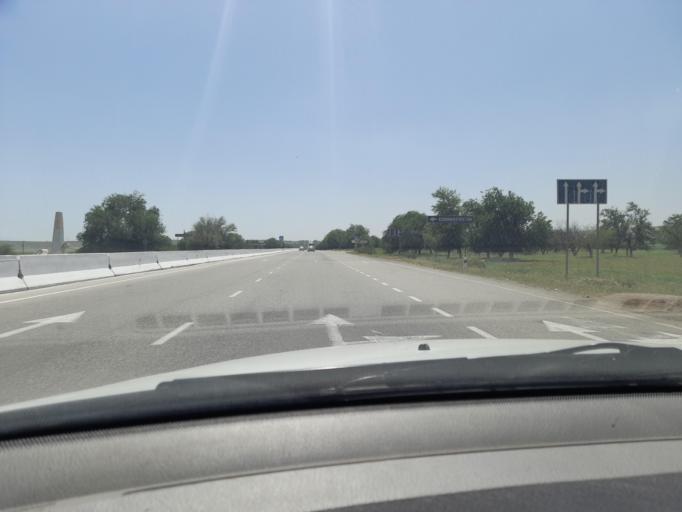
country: UZ
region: Samarqand
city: Bulung'ur
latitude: 39.8829
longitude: 67.4873
